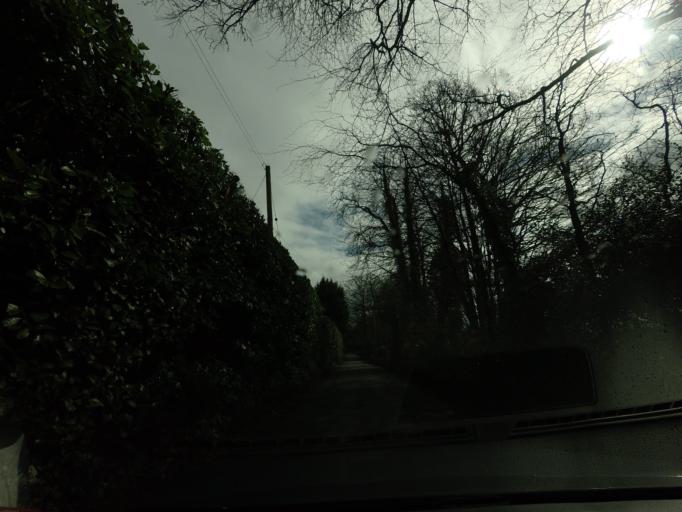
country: GB
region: England
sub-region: Kent
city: Borough Green
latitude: 51.2651
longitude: 0.2759
